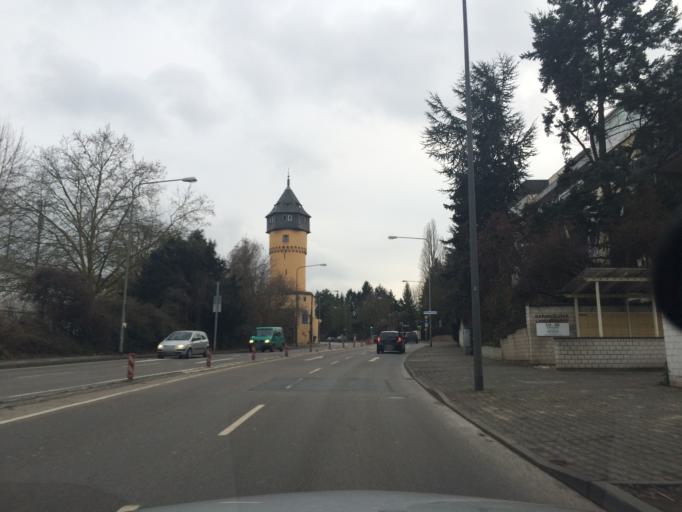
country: DE
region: Hesse
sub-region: Regierungsbezirk Darmstadt
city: Frankfurt am Main
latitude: 50.0894
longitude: 8.6911
